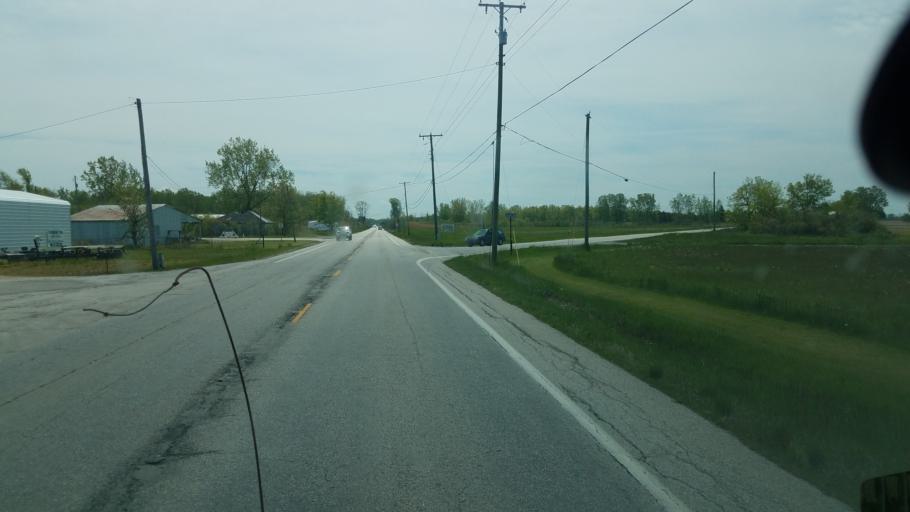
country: US
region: Ohio
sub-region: Ottawa County
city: Oak Harbor
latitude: 41.5748
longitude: -83.0872
